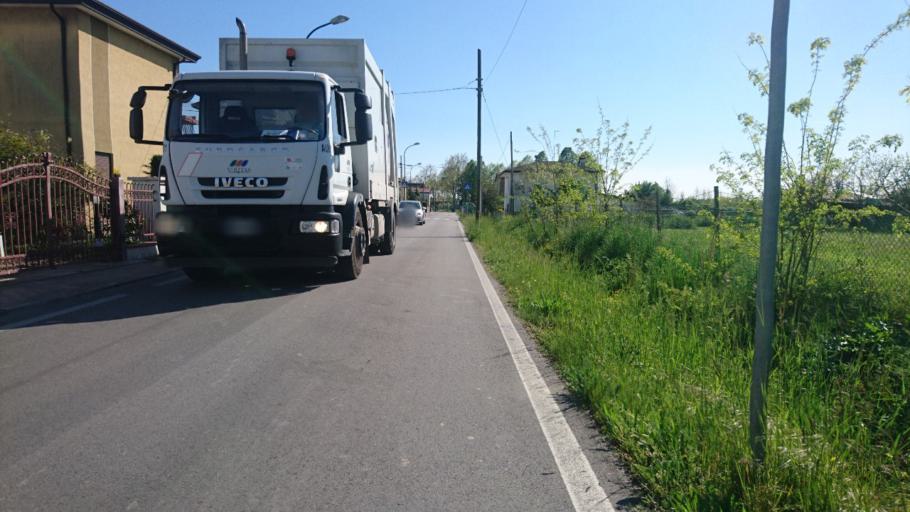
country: IT
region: Veneto
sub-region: Provincia di Venezia
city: Dese
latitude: 45.5251
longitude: 12.2681
